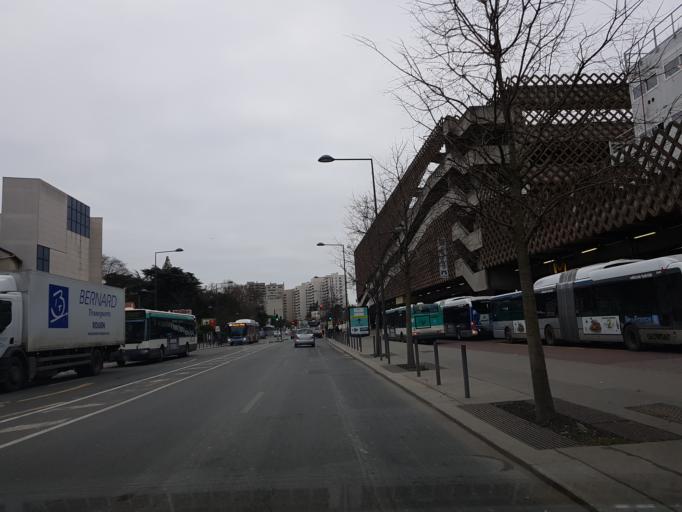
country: FR
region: Ile-de-France
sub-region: Departement du Val-de-Marne
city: Villejuif
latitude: 48.7881
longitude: 2.3680
